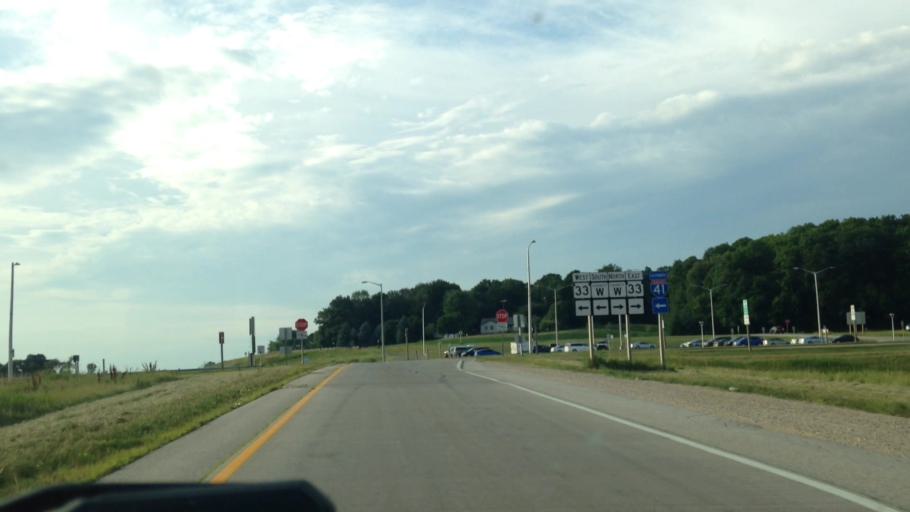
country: US
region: Wisconsin
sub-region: Washington County
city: Slinger
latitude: 43.4234
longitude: -88.3351
